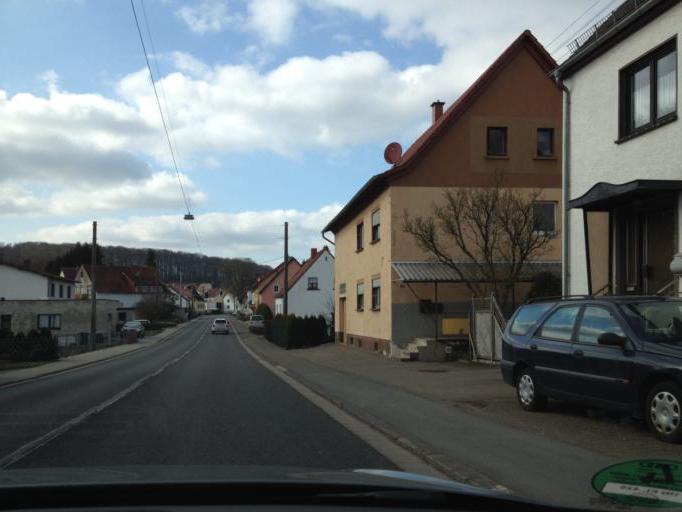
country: DE
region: Saarland
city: Oberthal
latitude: 49.4701
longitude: 7.1049
